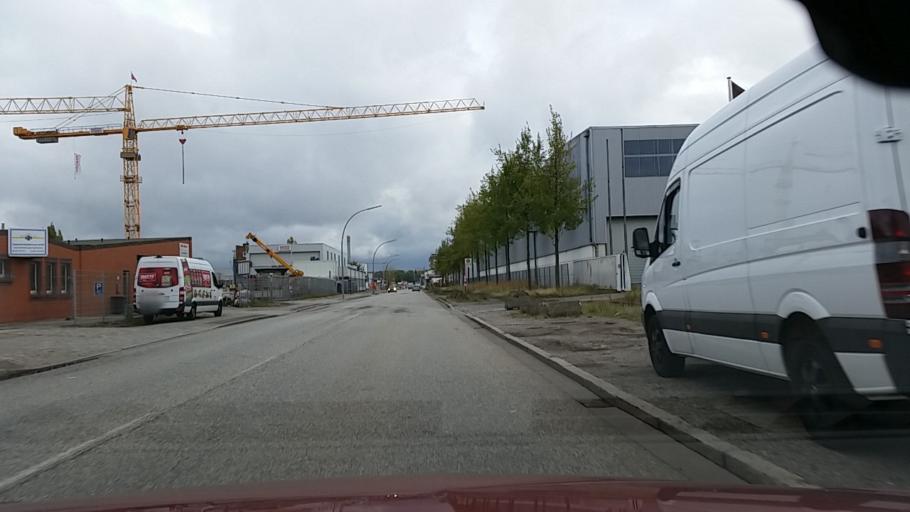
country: DE
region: Hamburg
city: Marienthal
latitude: 53.5304
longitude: 10.0911
